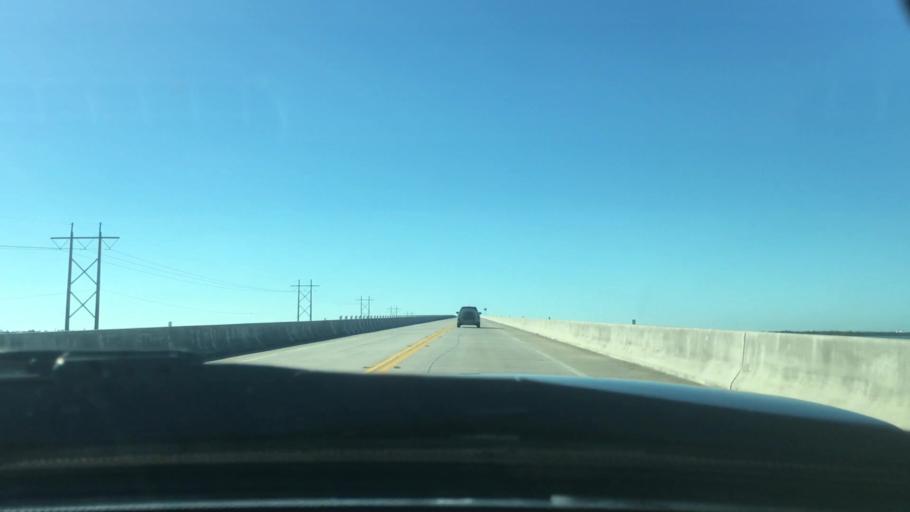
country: US
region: Florida
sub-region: Monroe County
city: Big Pine Key
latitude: 24.6602
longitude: -81.4234
